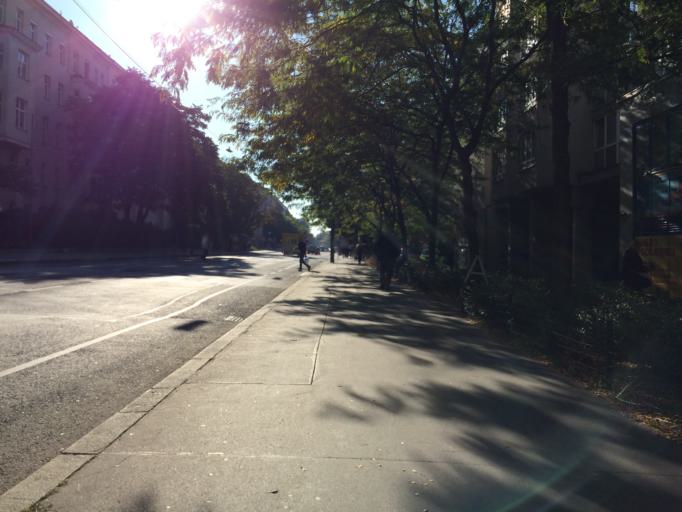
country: AT
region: Vienna
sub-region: Wien Stadt
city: Vienna
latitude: 48.2251
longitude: 16.4005
